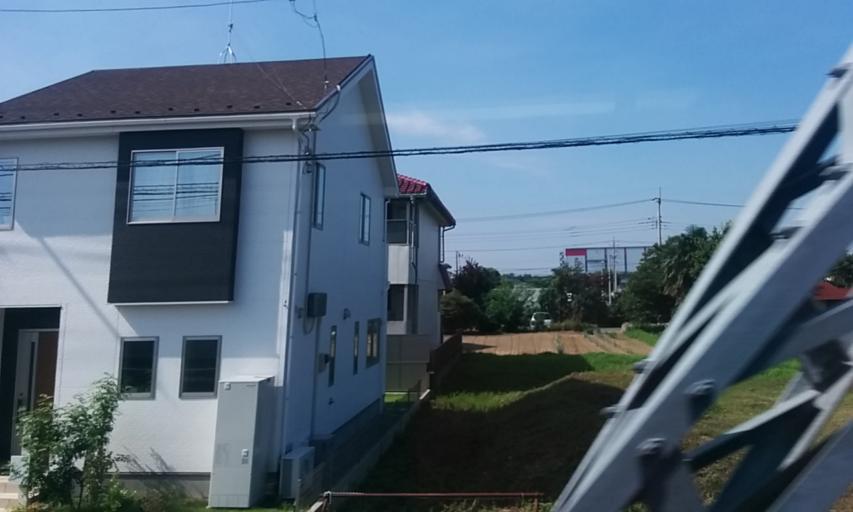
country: JP
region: Saitama
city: Kazo
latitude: 36.1168
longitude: 139.6129
